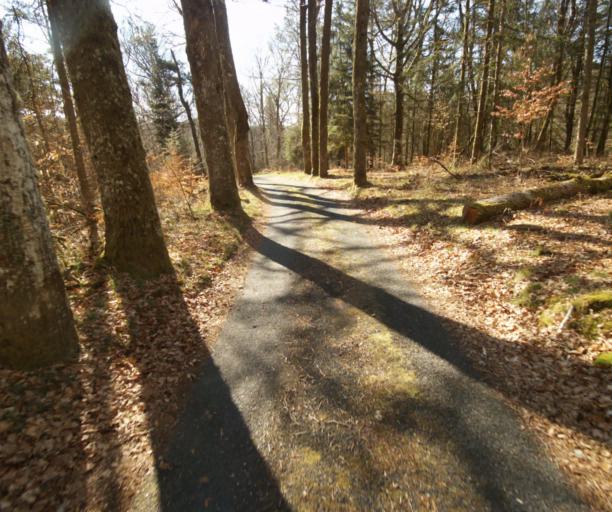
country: FR
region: Limousin
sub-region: Departement de la Correze
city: Laguenne
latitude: 45.2373
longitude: 1.9144
